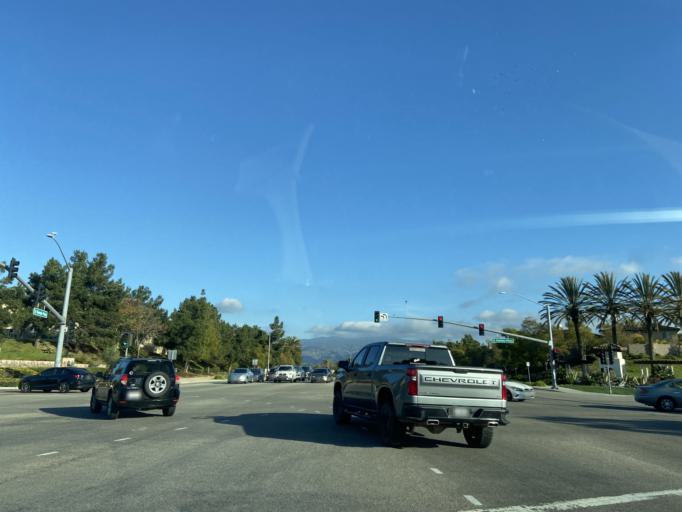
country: US
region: California
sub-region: San Diego County
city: Bonita
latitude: 32.6277
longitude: -116.9649
